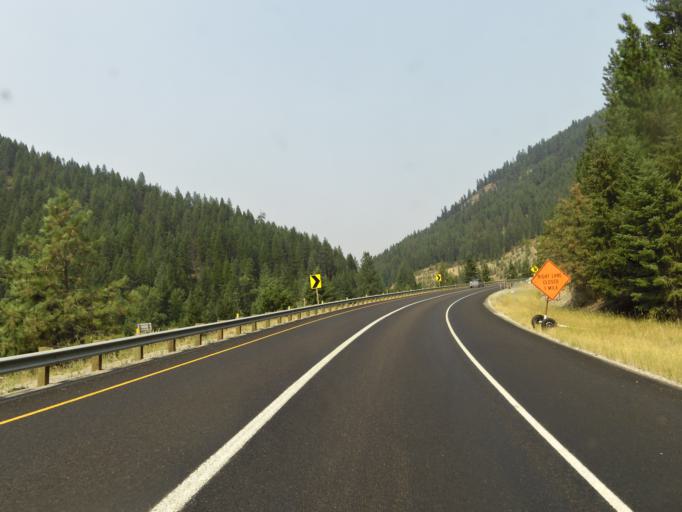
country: US
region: Montana
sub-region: Sanders County
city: Thompson Falls
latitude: 47.3281
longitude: -115.2567
